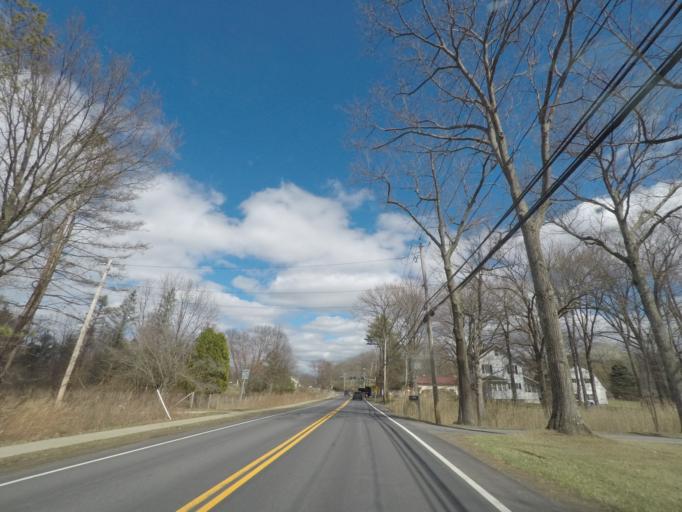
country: US
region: New York
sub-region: Albany County
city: Delmar
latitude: 42.6015
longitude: -73.8139
